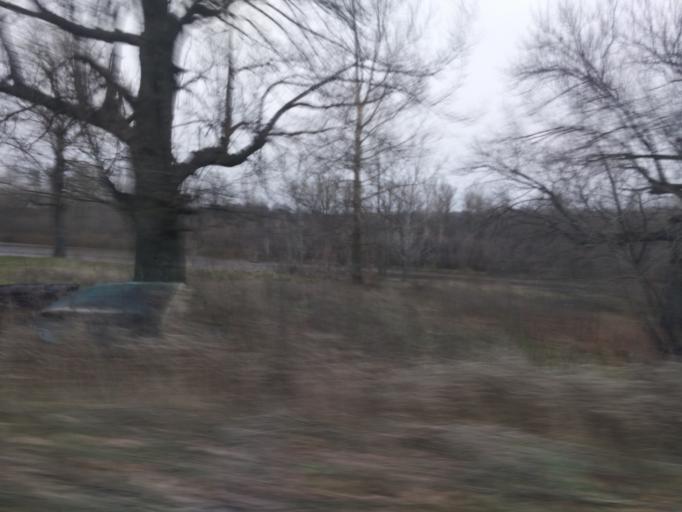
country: RU
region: Kirov
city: Krasnaya Polyana
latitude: 56.2451
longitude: 51.1922
